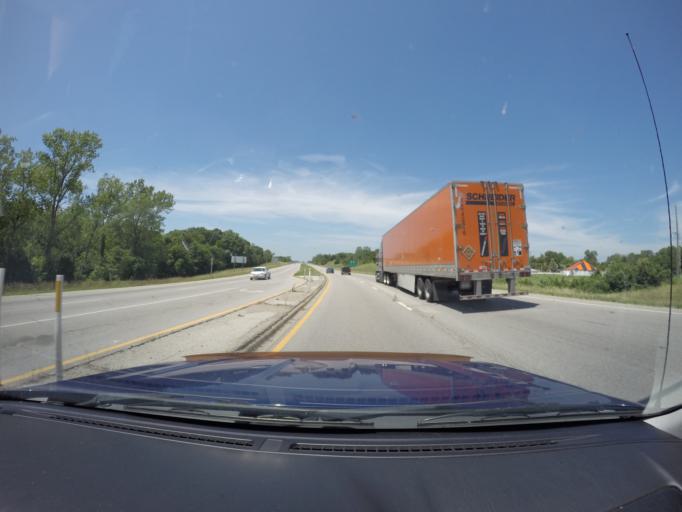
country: US
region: Kansas
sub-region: Wyandotte County
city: Bonner Springs
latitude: 39.1048
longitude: -94.8825
